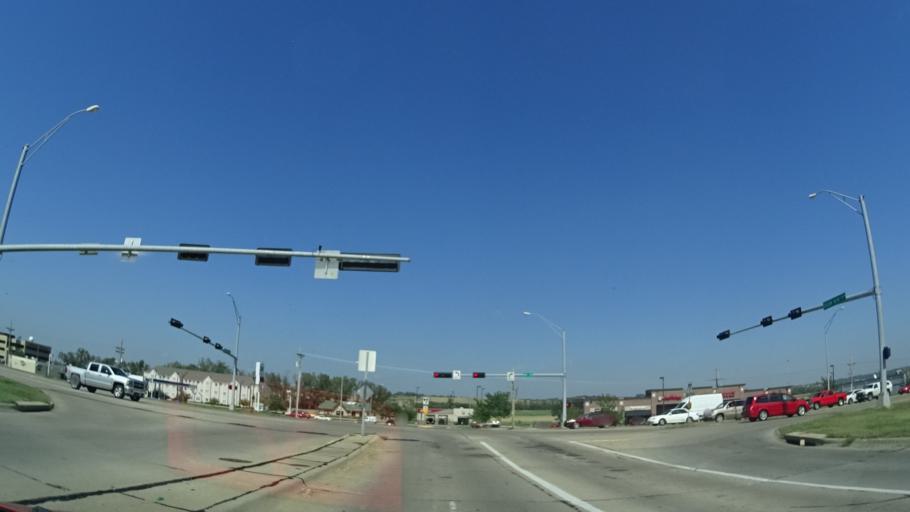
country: US
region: Nebraska
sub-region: Sarpy County
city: Offutt Air Force Base
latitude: 41.1371
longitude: -95.9571
